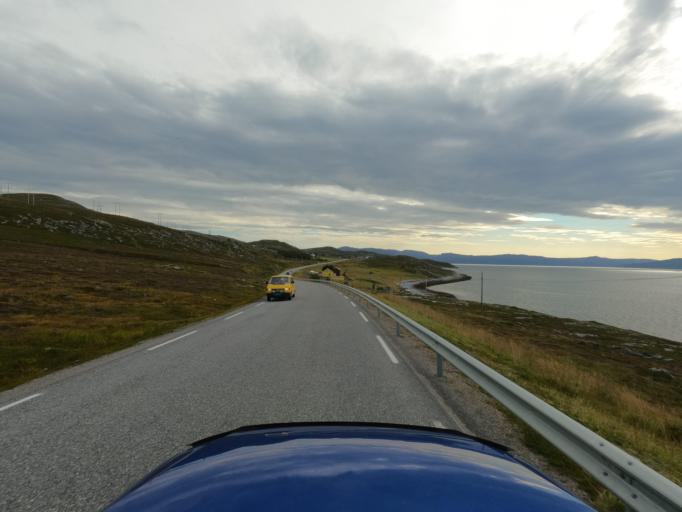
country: NO
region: Finnmark Fylke
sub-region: Hammerfest
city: Rypefjord
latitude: 70.5546
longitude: 23.7170
